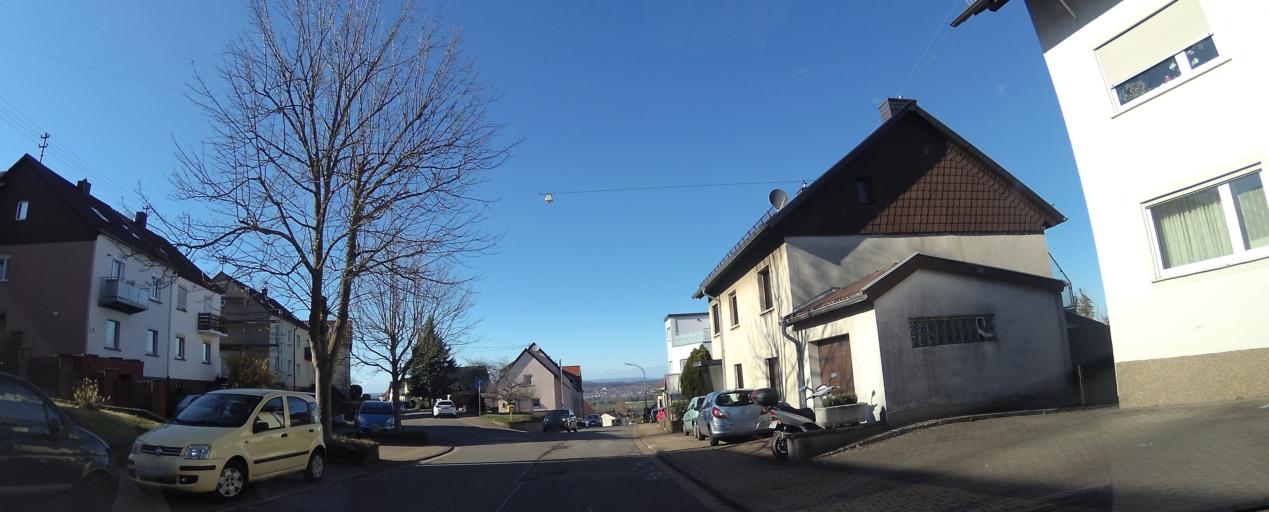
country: DE
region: Saarland
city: Riegelsberg
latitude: 49.3021
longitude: 6.9300
